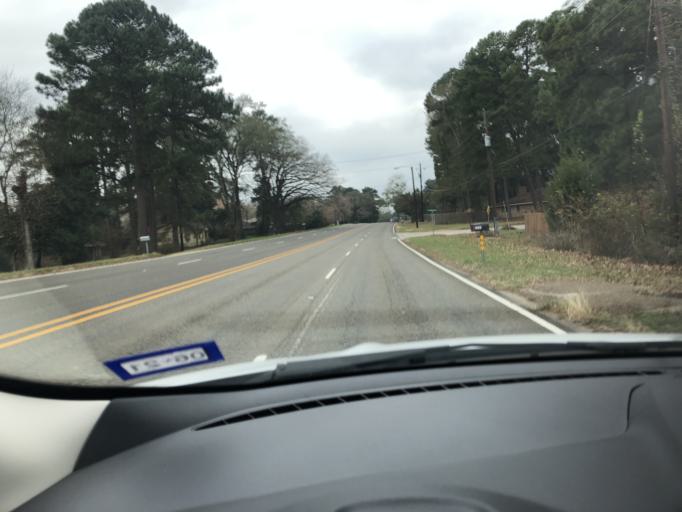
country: US
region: Texas
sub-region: Nacogdoches County
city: Nacogdoches
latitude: 31.6370
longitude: -94.6249
